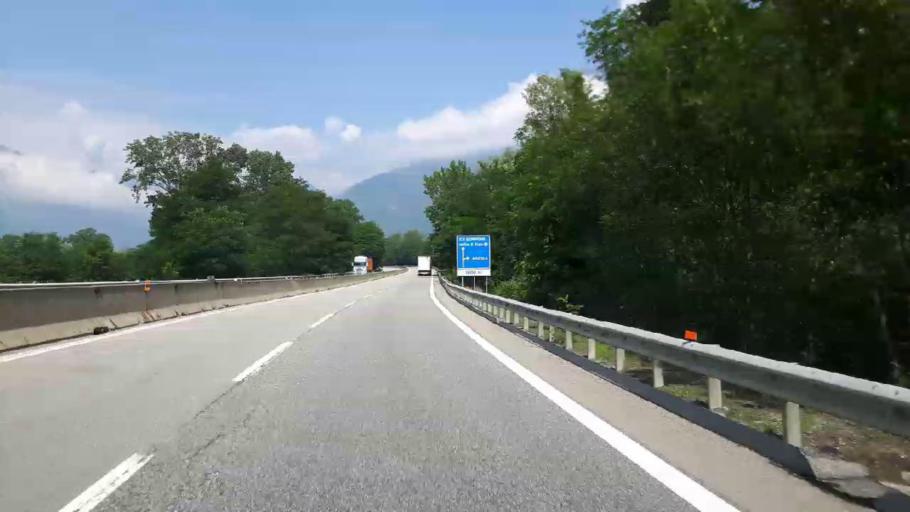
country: IT
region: Piedmont
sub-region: Provincia Verbano-Cusio-Ossola
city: Anzola d'Ossola
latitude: 45.9864
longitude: 8.3673
